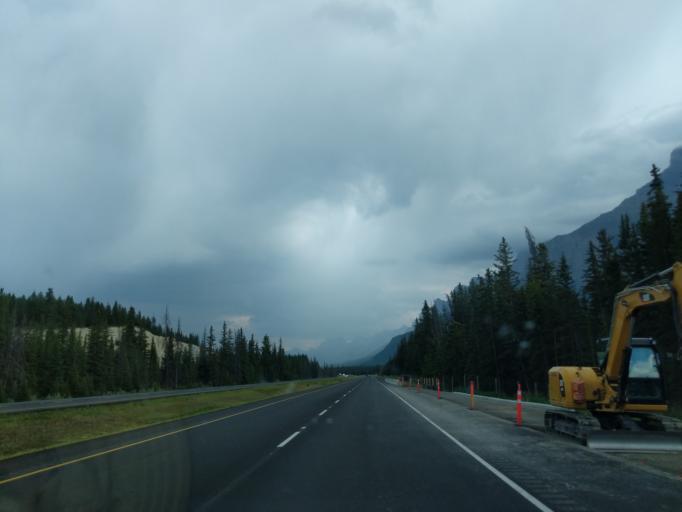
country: CA
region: Alberta
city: Banff
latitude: 51.1893
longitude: -115.4904
